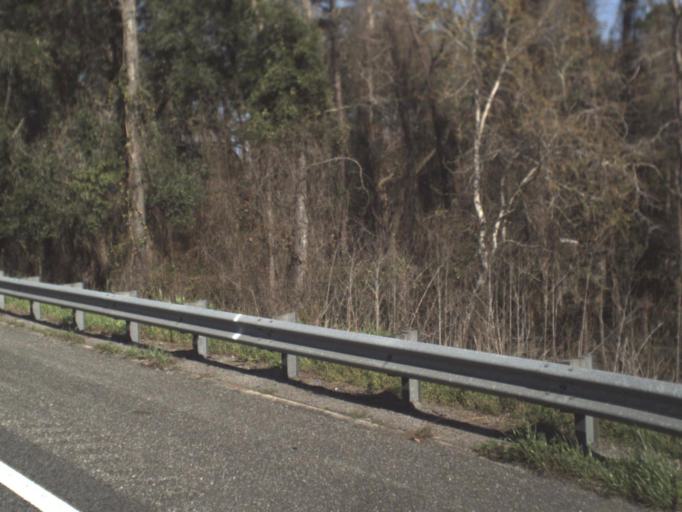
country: US
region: Florida
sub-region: Leon County
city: Tallahassee
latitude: 30.4791
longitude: -84.1460
